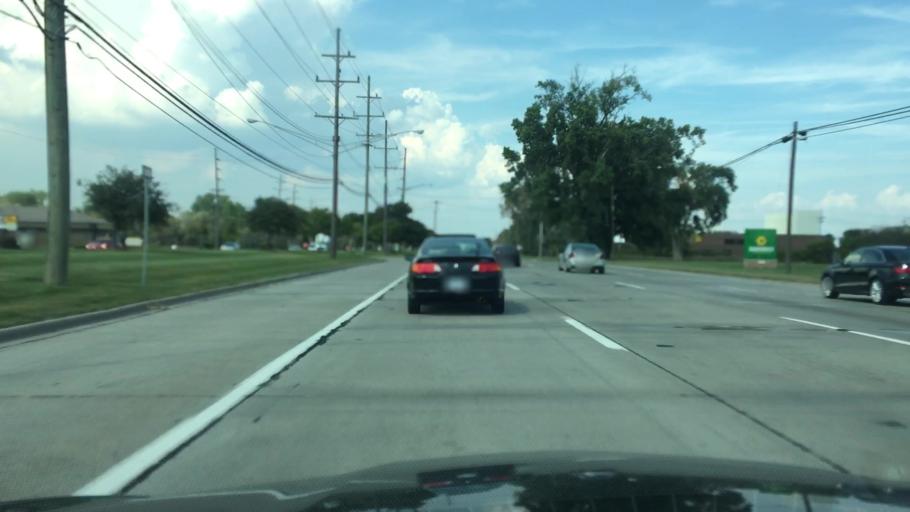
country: US
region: Michigan
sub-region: Macomb County
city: Sterling Heights
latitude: 42.5566
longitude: -83.0486
